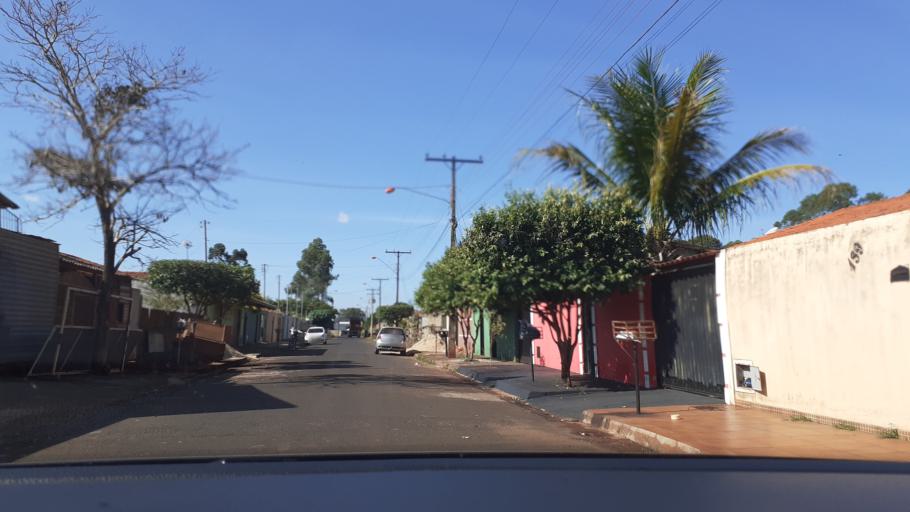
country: BR
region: Goias
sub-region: Itumbiara
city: Itumbiara
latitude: -18.4124
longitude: -49.2533
